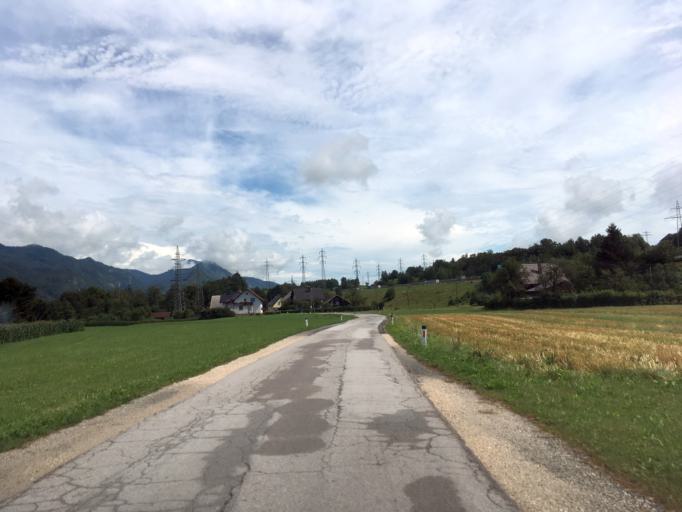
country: SI
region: Jesenice
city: Slovenski Javornik
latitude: 46.4162
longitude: 14.0967
